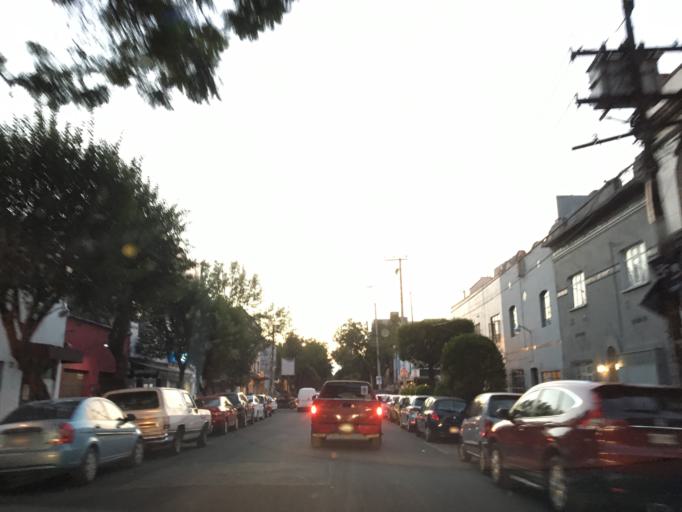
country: MX
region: Mexico City
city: Benito Juarez
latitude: 19.4125
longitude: -99.1565
